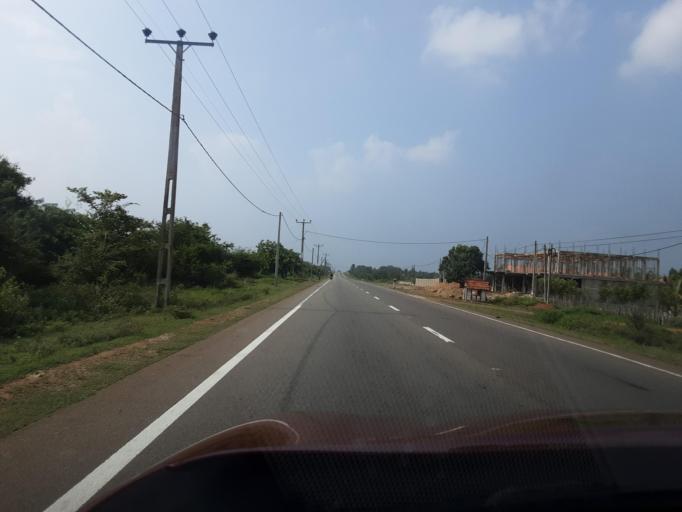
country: LK
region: Northern Province
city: Kilinochchi
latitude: 9.0841
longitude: 80.4784
